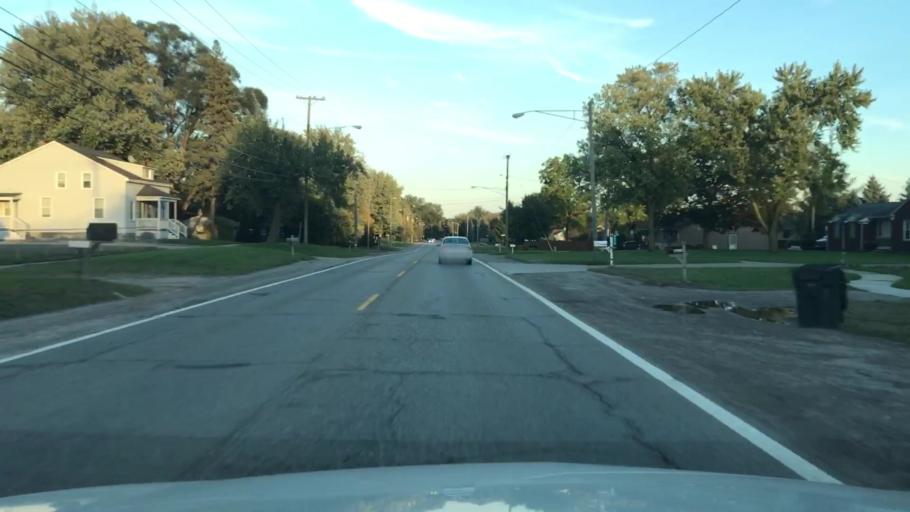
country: US
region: Michigan
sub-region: Macomb County
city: Utica
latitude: 42.6395
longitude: -83.0688
